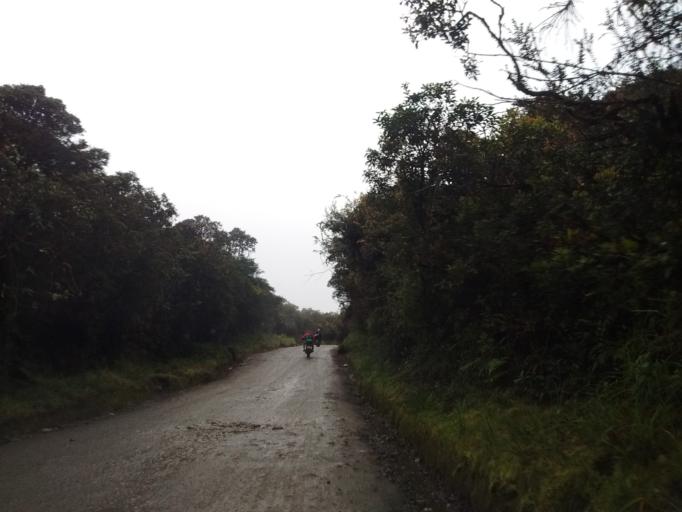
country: CO
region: Cauca
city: Paispamba
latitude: 2.1455
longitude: -76.4315
